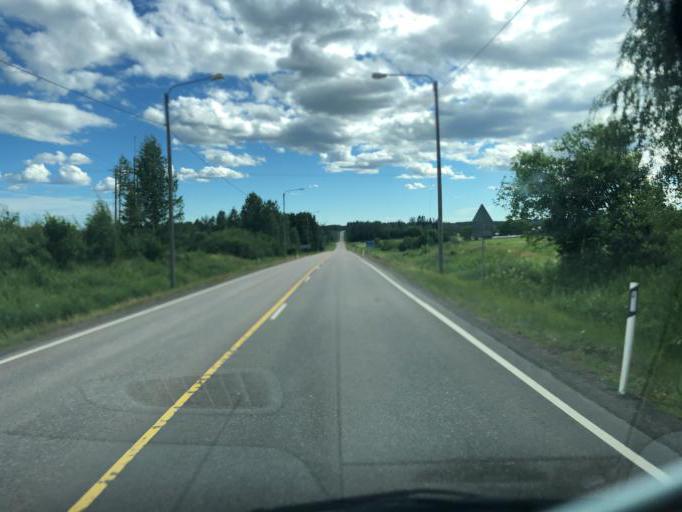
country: FI
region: Southern Savonia
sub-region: Mikkeli
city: Maentyharju
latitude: 61.0887
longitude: 27.0664
